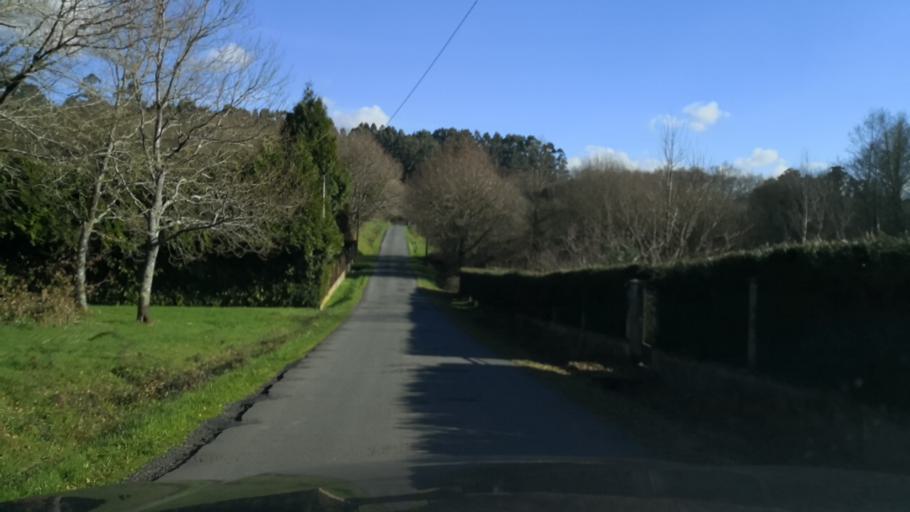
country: ES
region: Galicia
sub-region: Provincia da Coruna
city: Ribeira
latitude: 42.7121
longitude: -8.4337
